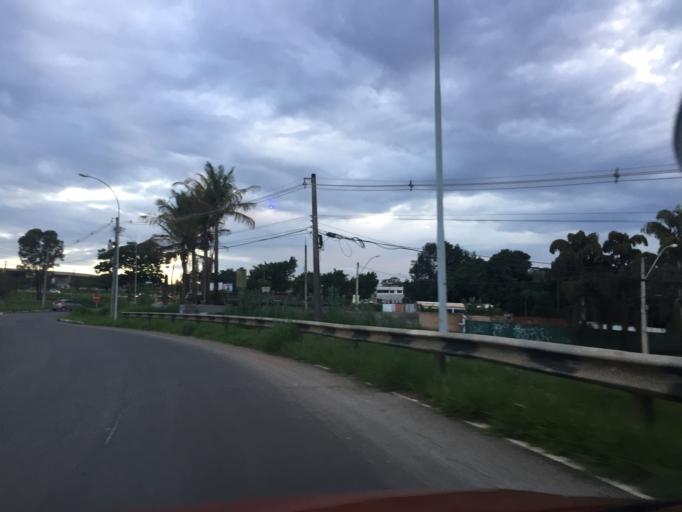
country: BR
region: Federal District
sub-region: Brasilia
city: Brasilia
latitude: -15.8735
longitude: -47.9601
